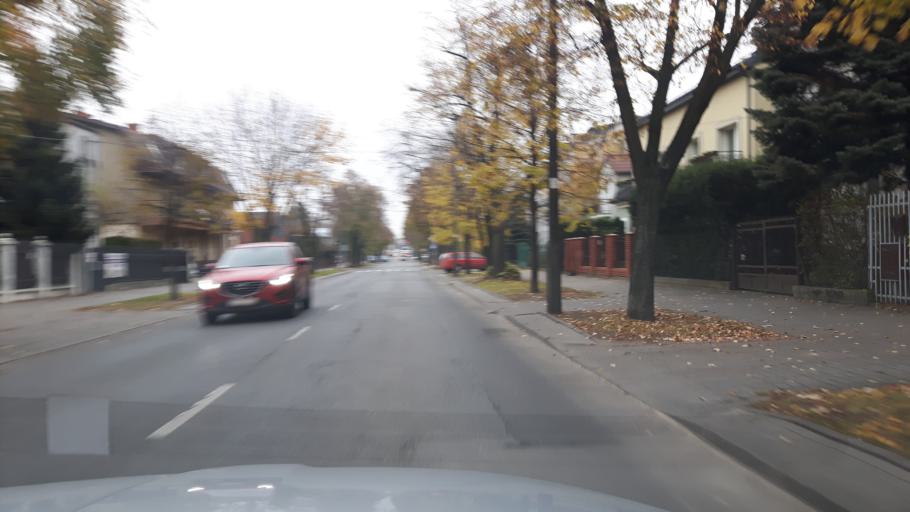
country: PL
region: Masovian Voivodeship
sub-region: Warszawa
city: Targowek
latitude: 52.2785
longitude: 21.0619
